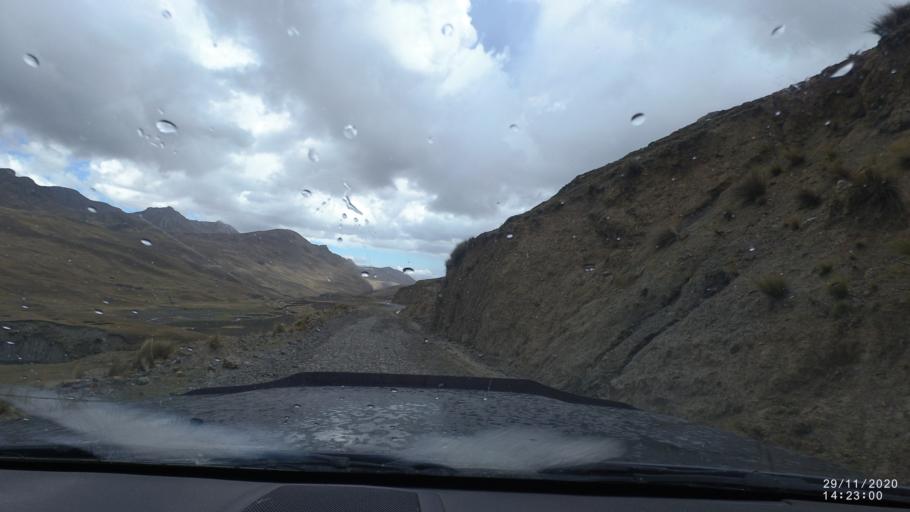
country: BO
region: Cochabamba
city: Sipe Sipe
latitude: -17.2538
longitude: -66.3862
